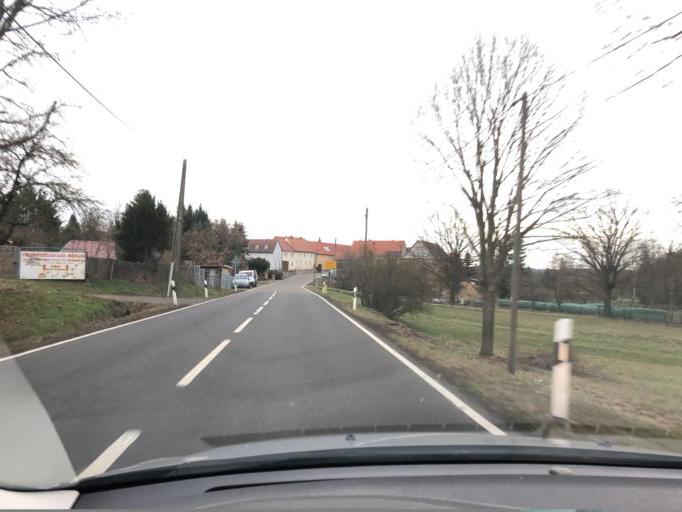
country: DE
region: Saxony-Anhalt
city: Eckartsberga
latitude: 51.1548
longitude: 11.5647
